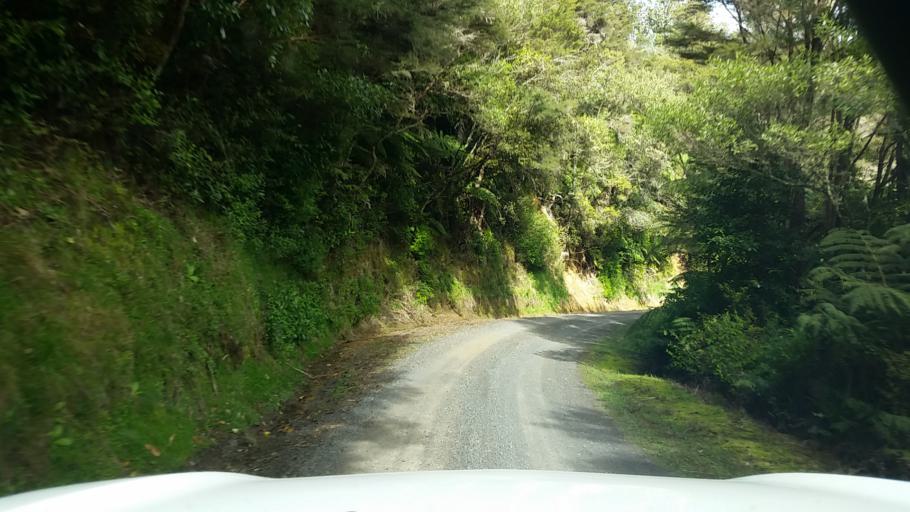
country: NZ
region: Waikato
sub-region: Hauraki District
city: Ngatea
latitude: -37.4676
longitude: 175.4558
